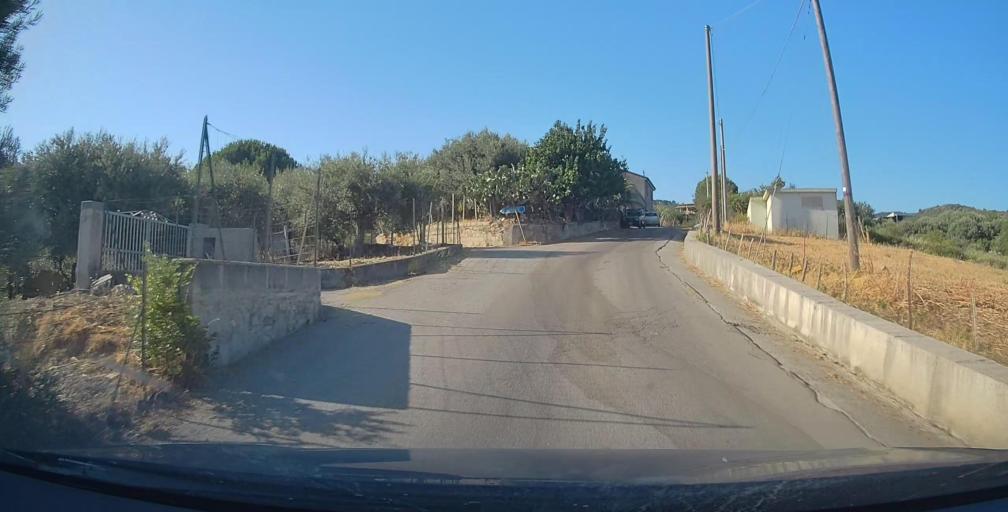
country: IT
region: Sicily
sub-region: Messina
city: San Piero Patti
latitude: 38.0645
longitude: 14.9894
